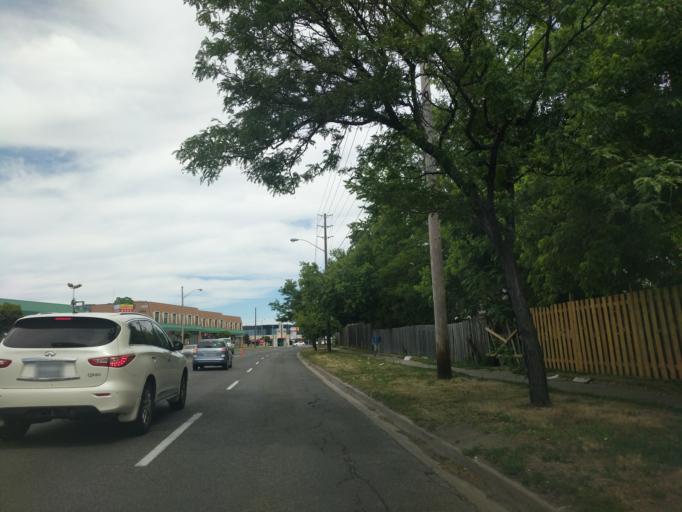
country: CA
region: Ontario
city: Scarborough
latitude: 43.8057
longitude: -79.2876
